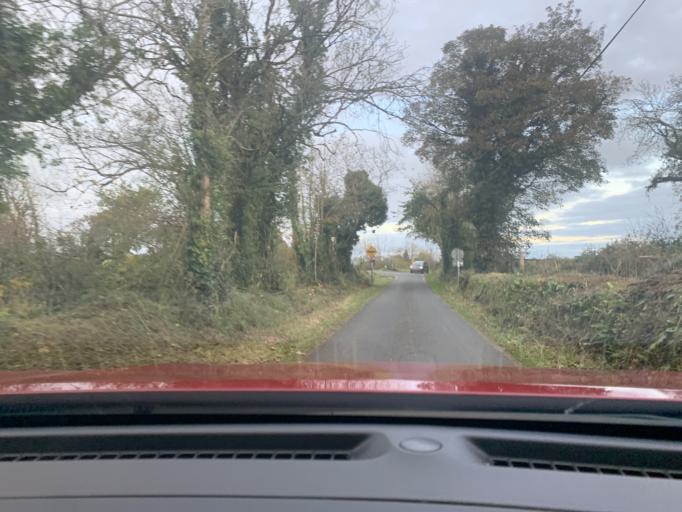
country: IE
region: Connaught
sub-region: Sligo
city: Tobercurry
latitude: 54.0917
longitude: -8.6735
